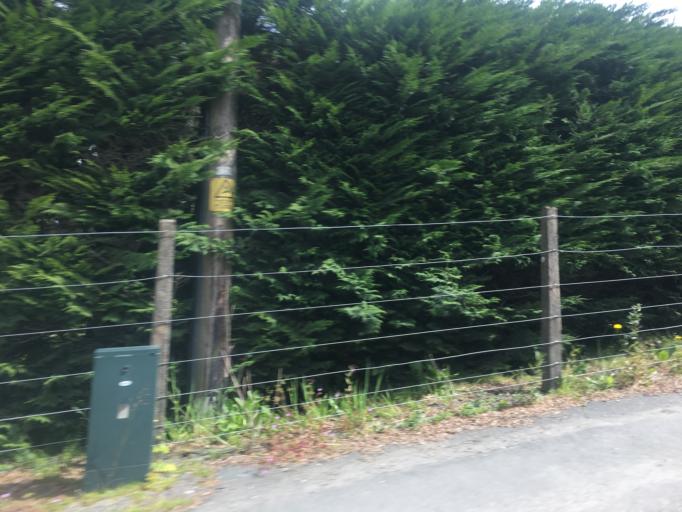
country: GB
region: Wales
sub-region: County of Ceredigion
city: Lampeter
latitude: 52.1196
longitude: -4.0790
